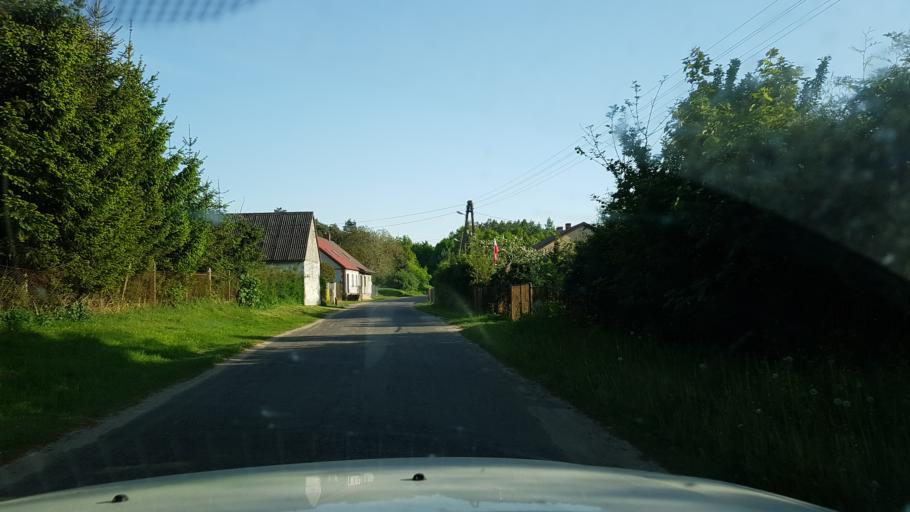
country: PL
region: West Pomeranian Voivodeship
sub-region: Powiat lobeski
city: Dobra
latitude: 53.6109
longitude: 15.3295
